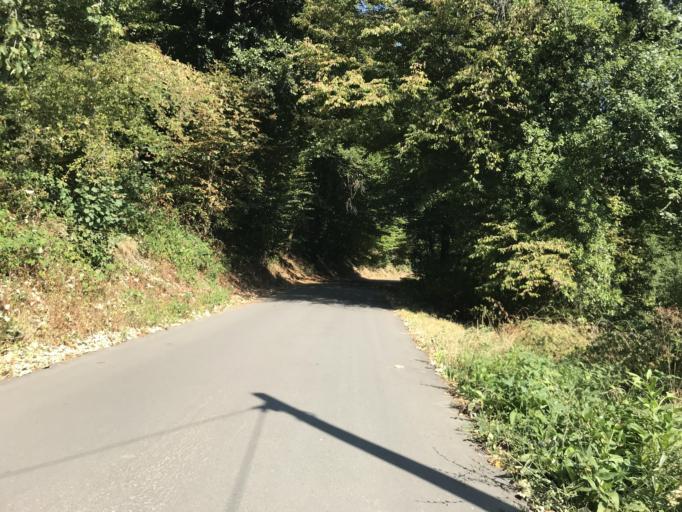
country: DE
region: Hesse
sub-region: Regierungsbezirk Darmstadt
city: Kiedrich
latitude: 50.0475
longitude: 8.0950
